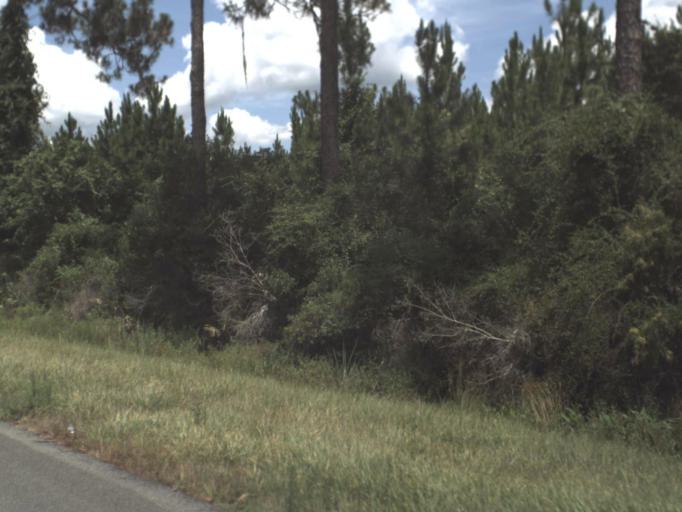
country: US
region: Florida
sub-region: Taylor County
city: Perry
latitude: 30.0906
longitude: -83.6781
